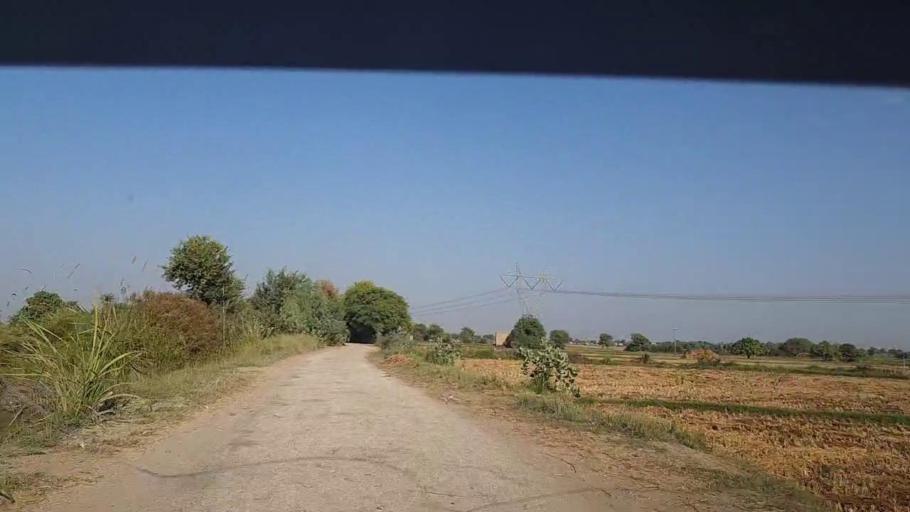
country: PK
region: Sindh
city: Larkana
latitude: 27.6217
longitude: 68.2486
